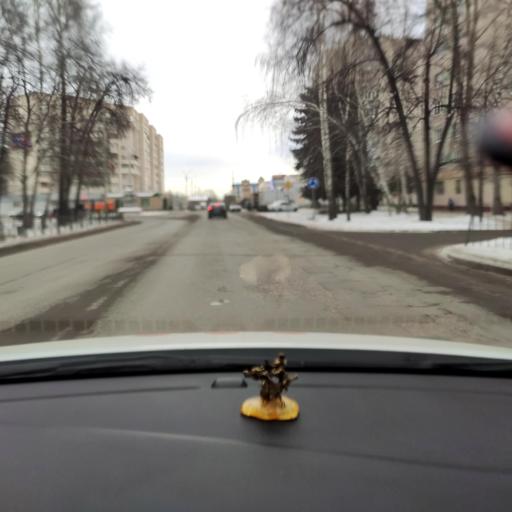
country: RU
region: Tatarstan
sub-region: Zelenodol'skiy Rayon
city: Zelenodolsk
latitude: 55.8454
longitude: 48.5221
